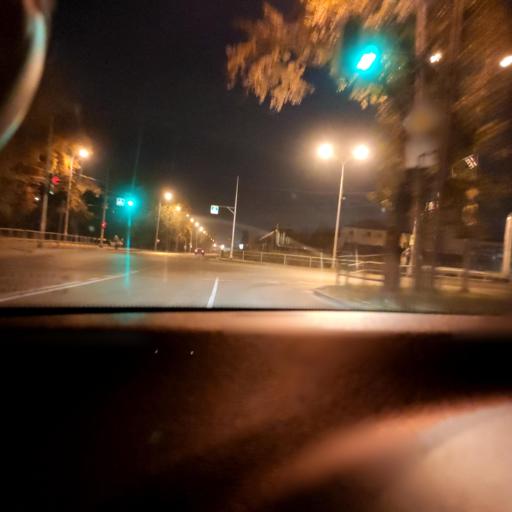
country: RU
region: Samara
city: Smyshlyayevka
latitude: 53.2146
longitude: 50.2933
